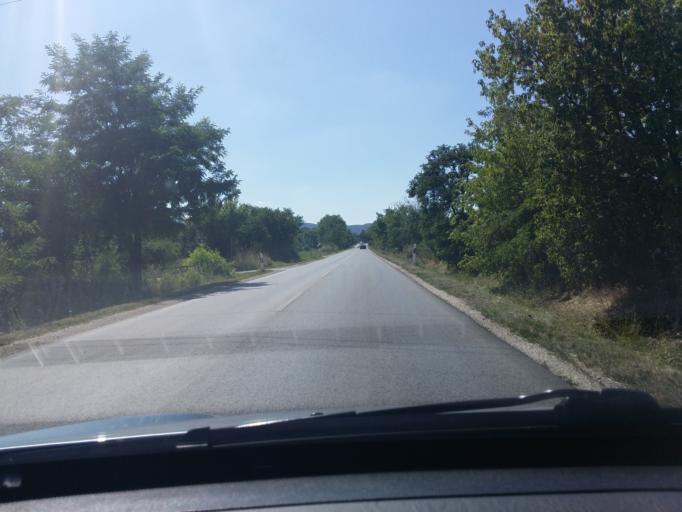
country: HU
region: Pest
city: Pomaz
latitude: 47.6457
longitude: 19.0487
